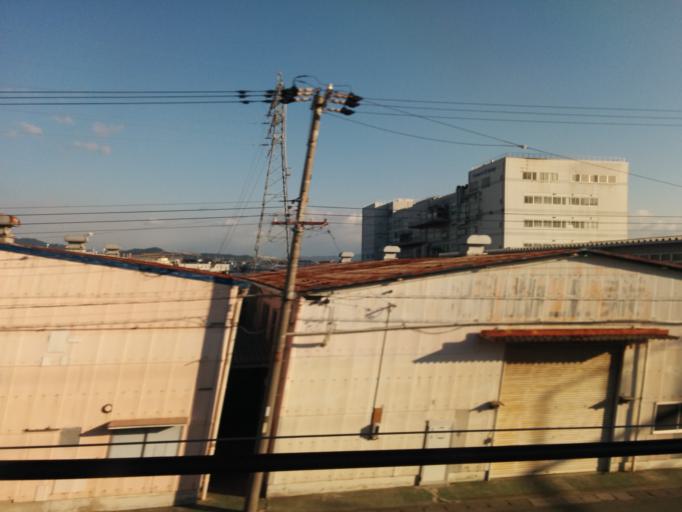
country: JP
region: Shizuoka
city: Kosai-shi
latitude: 34.7130
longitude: 137.4925
